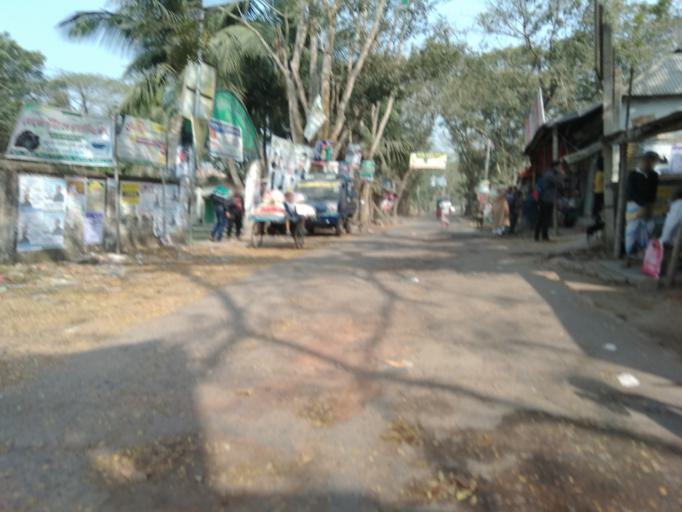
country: BD
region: Barisal
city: Mehendiganj
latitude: 22.9563
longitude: 90.4147
